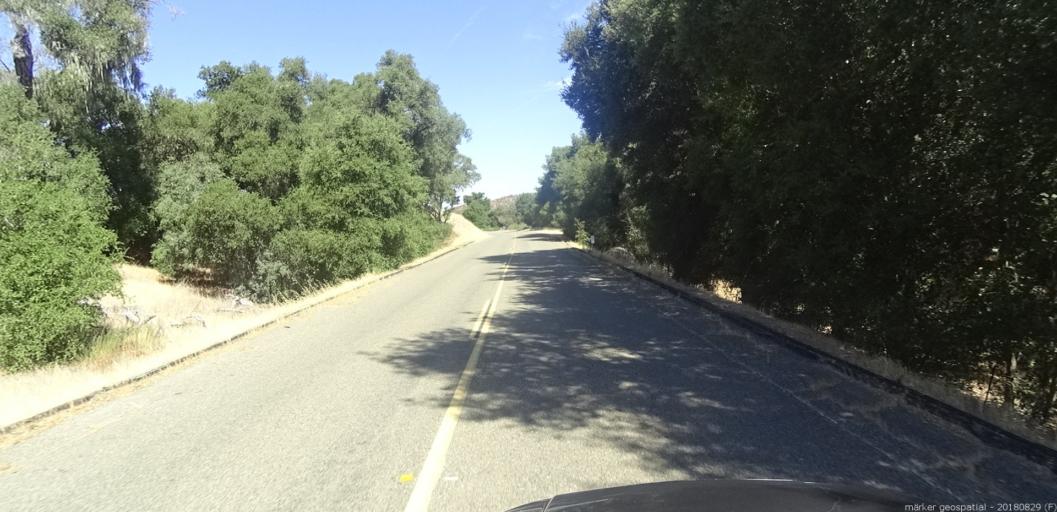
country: US
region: California
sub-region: San Luis Obispo County
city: Lake Nacimiento
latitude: 35.8011
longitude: -120.9752
